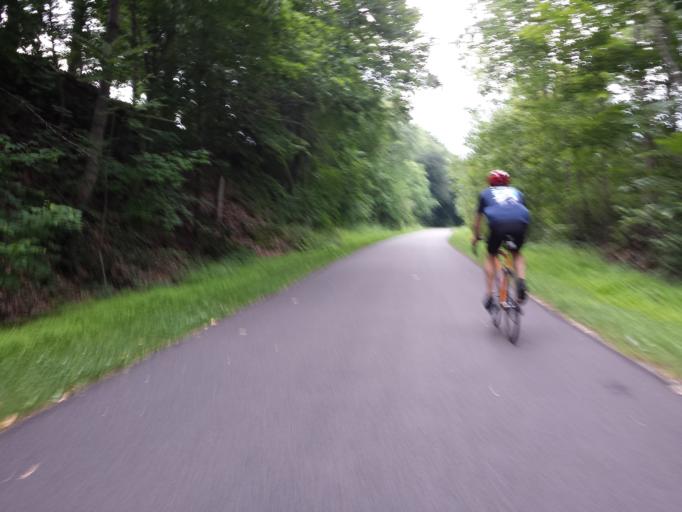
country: US
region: New York
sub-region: Dutchess County
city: Arlington
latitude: 41.6898
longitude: -73.8799
